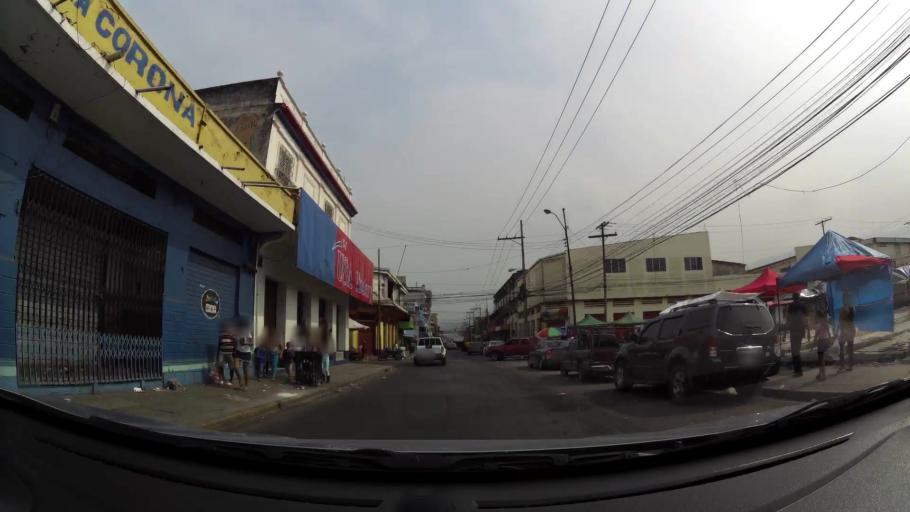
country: HN
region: Cortes
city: San Pedro Sula
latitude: 15.5016
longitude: -88.0249
